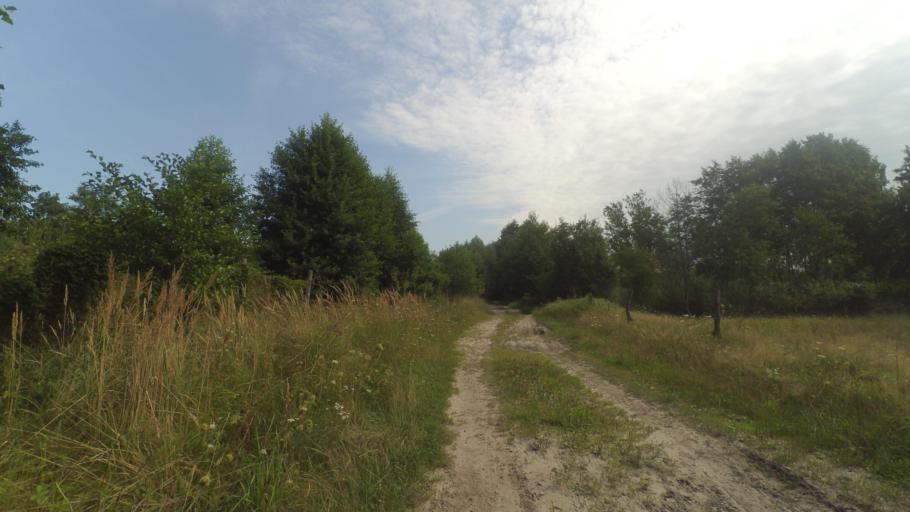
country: PL
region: Lublin Voivodeship
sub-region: Powiat wlodawski
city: Wlodawa
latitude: 51.5008
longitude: 23.6726
